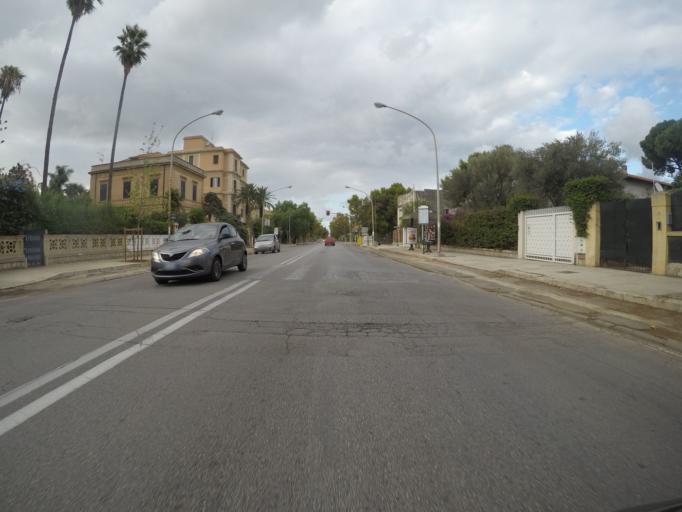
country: IT
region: Sicily
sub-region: Palermo
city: Palermo
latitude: 38.1930
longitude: 13.3324
